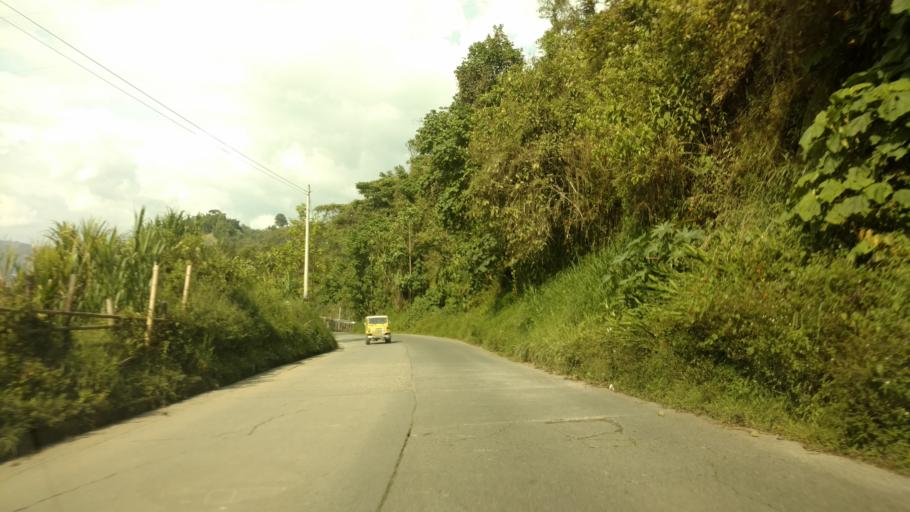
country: CO
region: Caldas
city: Manizales
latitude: 5.0888
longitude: -75.5169
